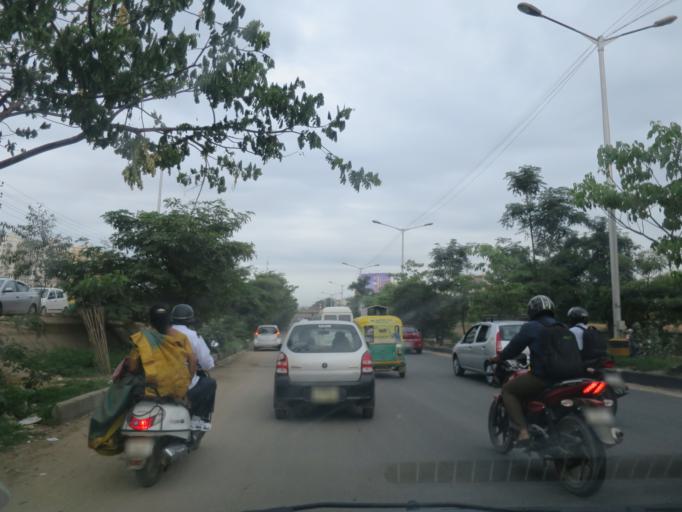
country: IN
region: Karnataka
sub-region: Bangalore Urban
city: Bangalore
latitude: 12.9747
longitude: 77.6977
